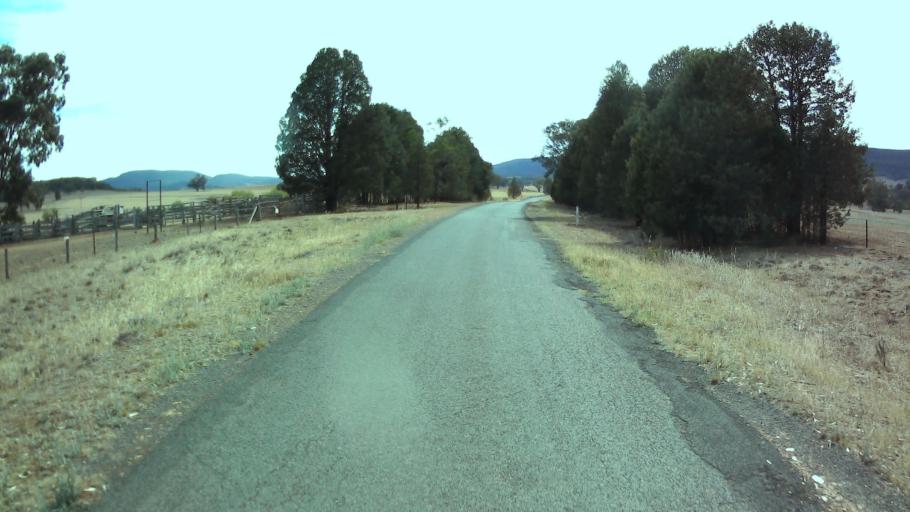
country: AU
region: New South Wales
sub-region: Weddin
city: Grenfell
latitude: -33.8305
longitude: 148.2769
